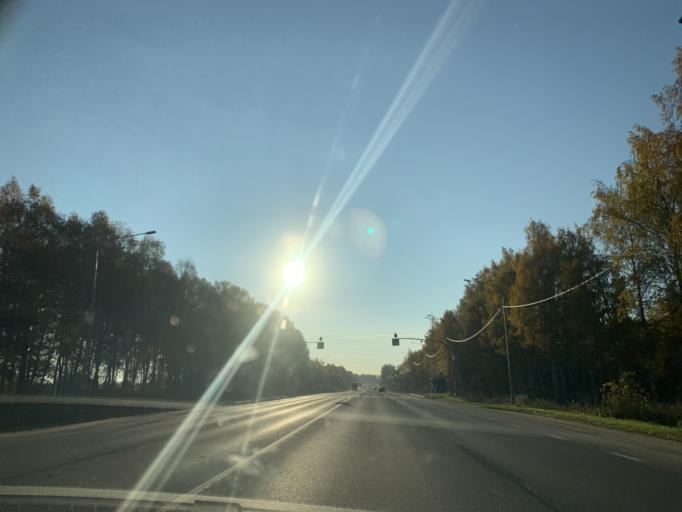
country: RU
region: Jaroslavl
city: Konstantinovskiy
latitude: 57.7456
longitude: 39.7147
